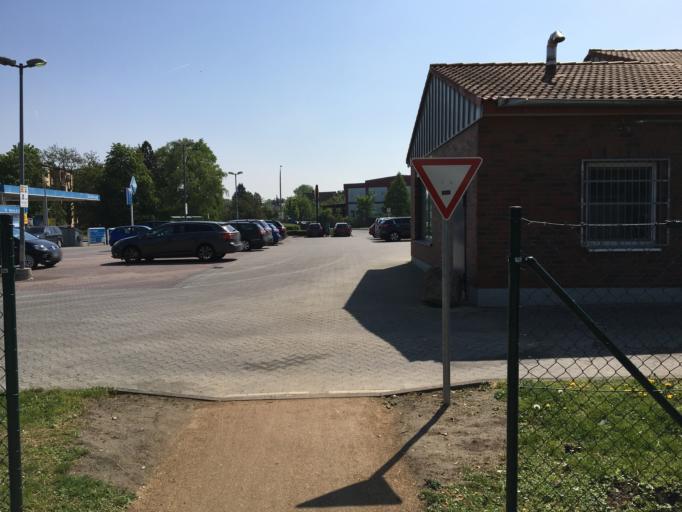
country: DE
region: Lower Saxony
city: Braunschweig
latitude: 52.2809
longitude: 10.5356
